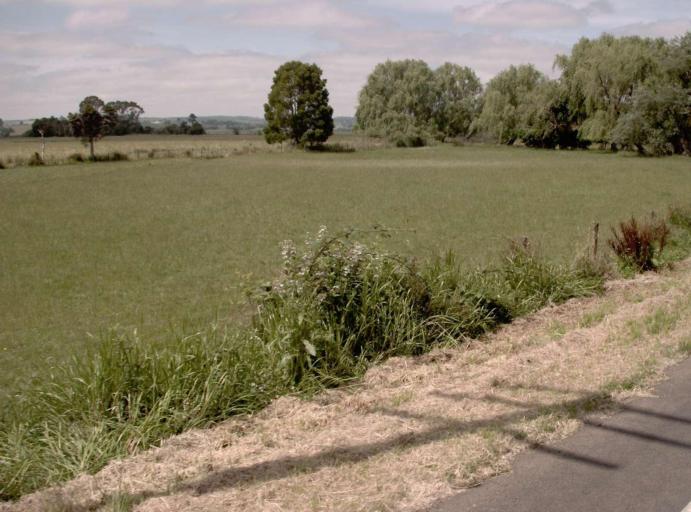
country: AU
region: Victoria
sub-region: Baw Baw
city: Warragul
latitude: -38.4553
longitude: 145.9746
